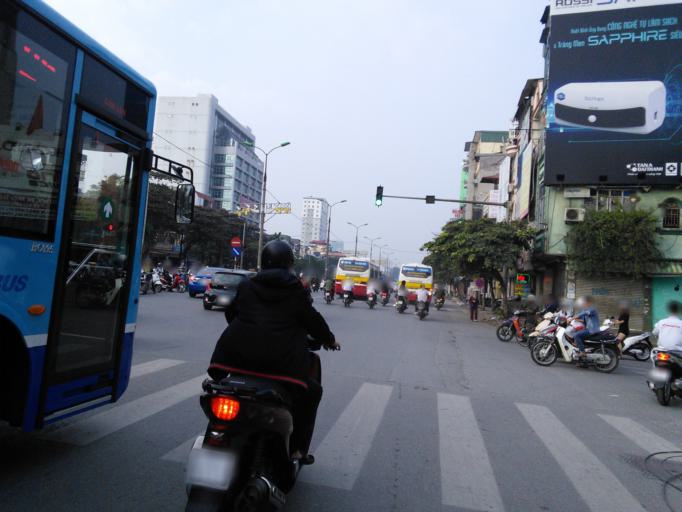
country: VN
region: Ha Noi
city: Hai BaTrung
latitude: 20.9919
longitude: 105.8413
